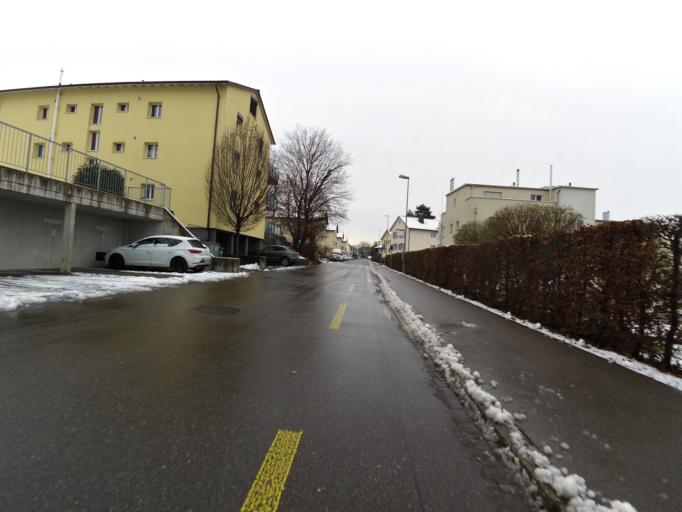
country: CH
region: Thurgau
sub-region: Frauenfeld District
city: Frauenfeld
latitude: 47.5618
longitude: 8.9077
